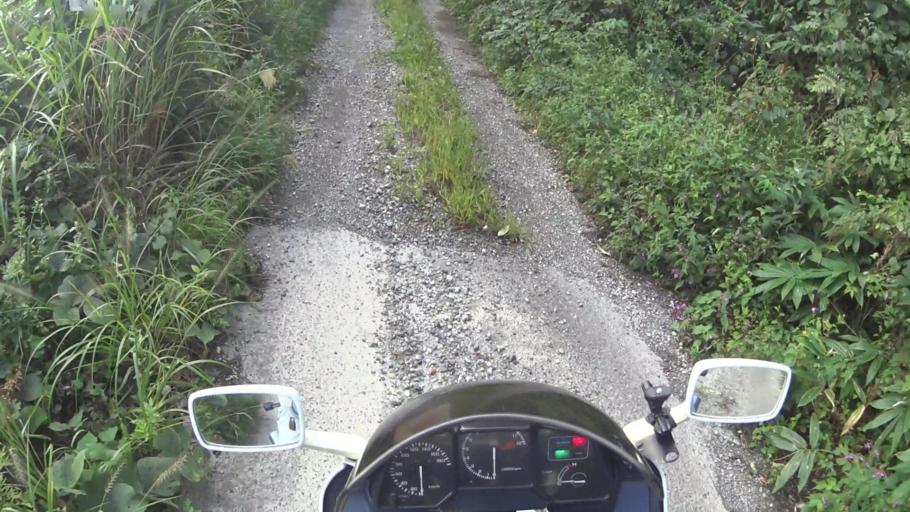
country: JP
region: Kyoto
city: Miyazu
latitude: 35.6391
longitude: 135.1822
